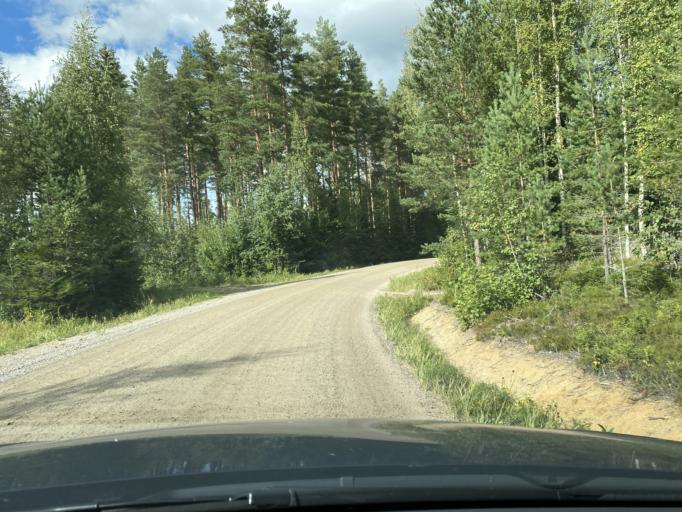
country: FI
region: Pirkanmaa
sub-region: Lounais-Pirkanmaa
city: Punkalaidun
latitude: 61.0796
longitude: 23.2677
